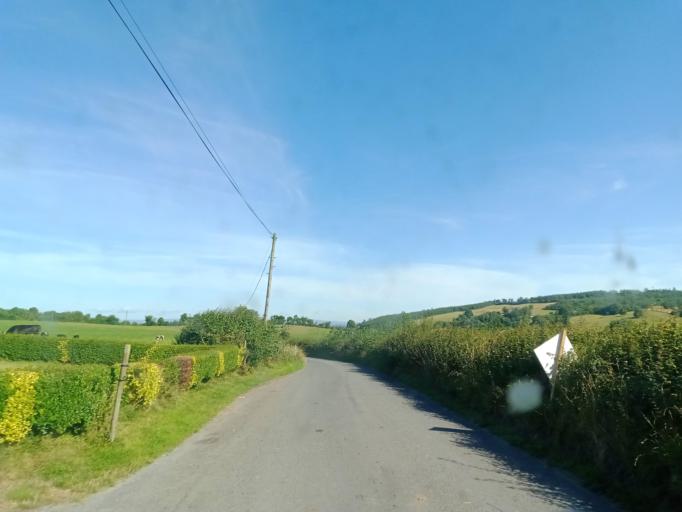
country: IE
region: Leinster
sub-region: Kilkenny
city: Ballyragget
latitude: 52.8033
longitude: -7.4314
